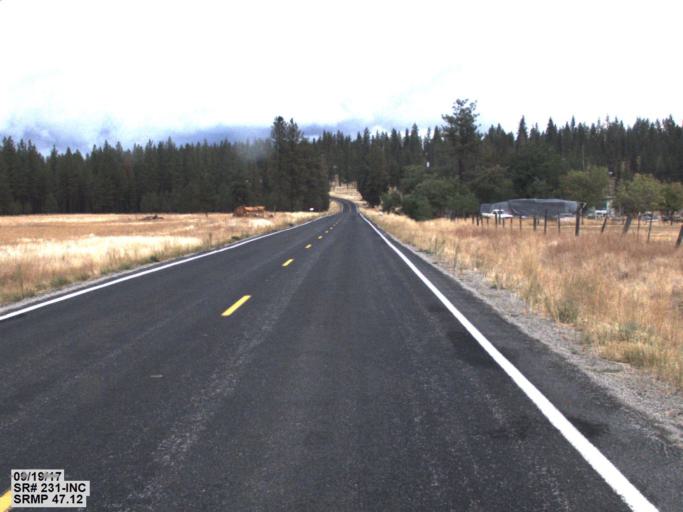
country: US
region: Washington
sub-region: Spokane County
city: Fairchild Air Force Base
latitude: 47.8701
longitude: -117.8401
